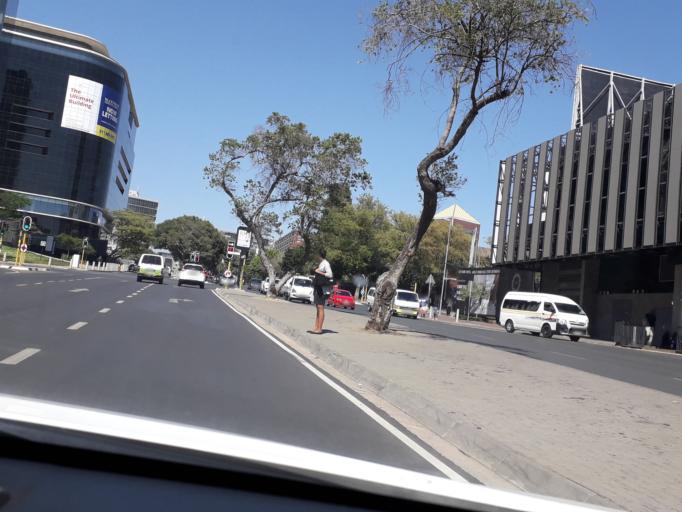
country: ZA
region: Gauteng
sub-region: City of Johannesburg Metropolitan Municipality
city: Johannesburg
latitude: -26.1087
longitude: 28.0568
